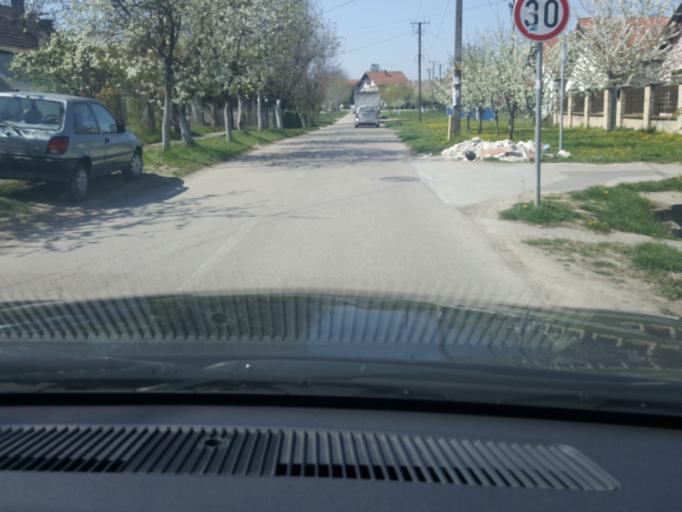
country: RS
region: Autonomna Pokrajina Vojvodina
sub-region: Zapadnobacki Okrug
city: Sombor
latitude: 45.7727
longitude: 19.0975
